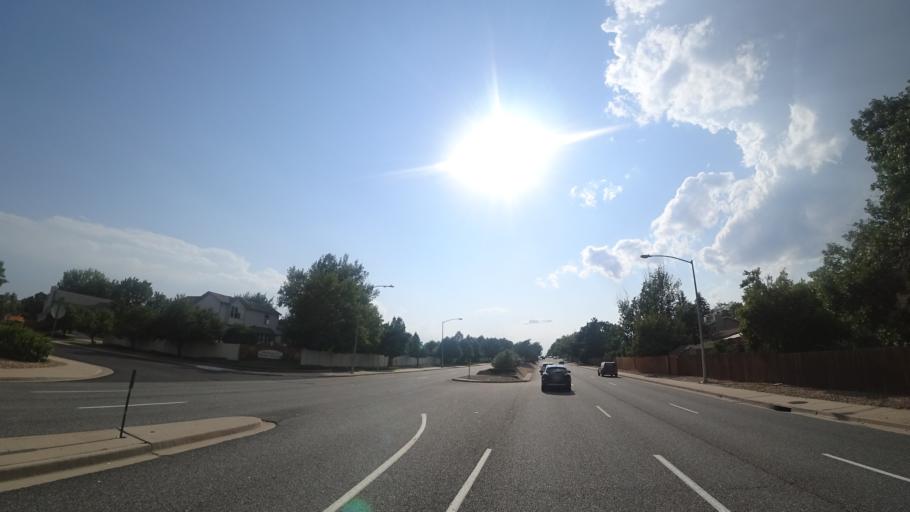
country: US
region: Colorado
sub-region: Arapahoe County
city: Dove Valley
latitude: 39.6386
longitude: -104.8039
